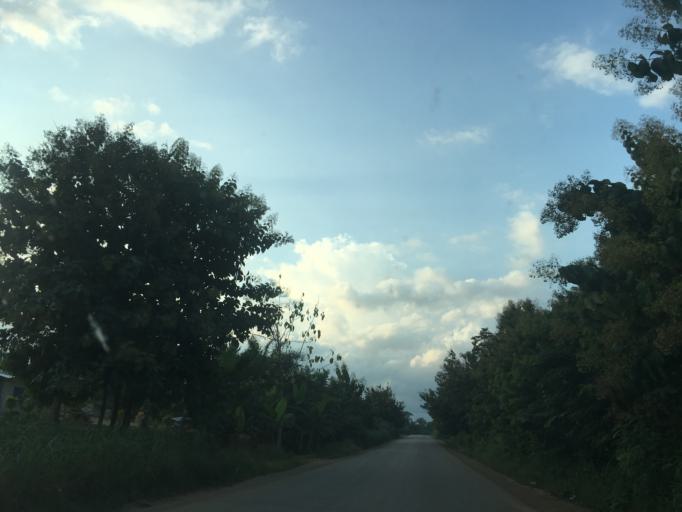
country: GH
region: Western
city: Bibiani
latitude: 6.6539
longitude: -2.4260
